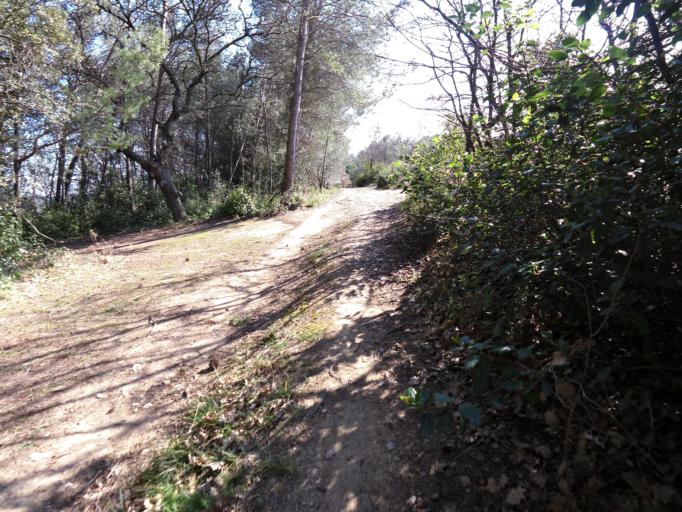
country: FR
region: Languedoc-Roussillon
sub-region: Departement du Gard
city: Aigues-Vives
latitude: 43.7518
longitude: 4.1730
